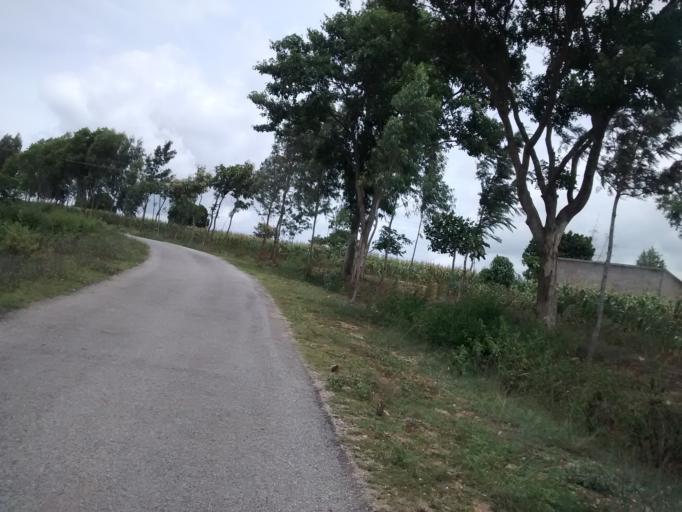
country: IN
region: Karnataka
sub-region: Hassan
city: Hassan
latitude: 12.9248
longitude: 76.1377
